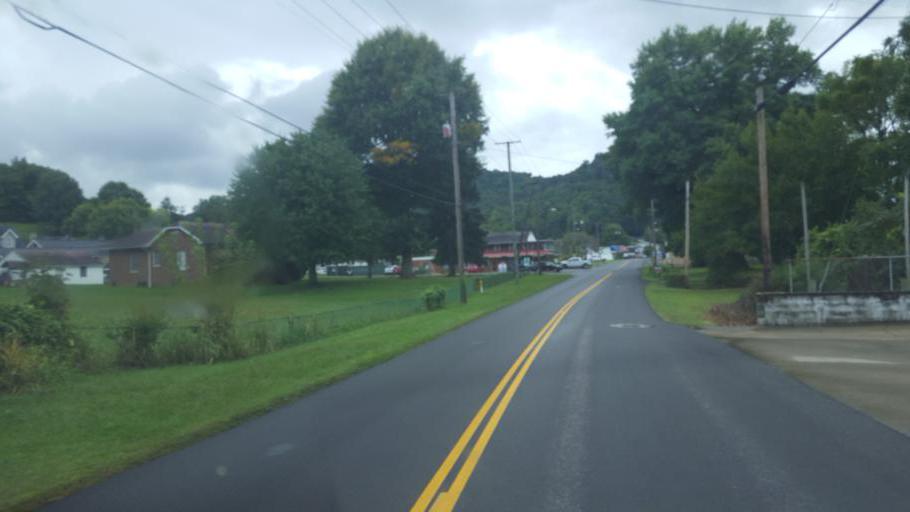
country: US
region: Ohio
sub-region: Scioto County
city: Rosemount
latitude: 38.7870
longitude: -82.9835
